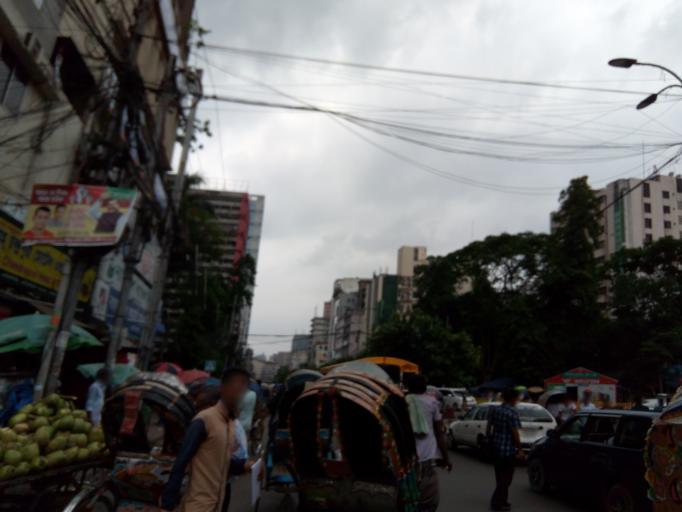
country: BD
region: Dhaka
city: Paltan
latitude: 23.7275
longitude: 90.4150
